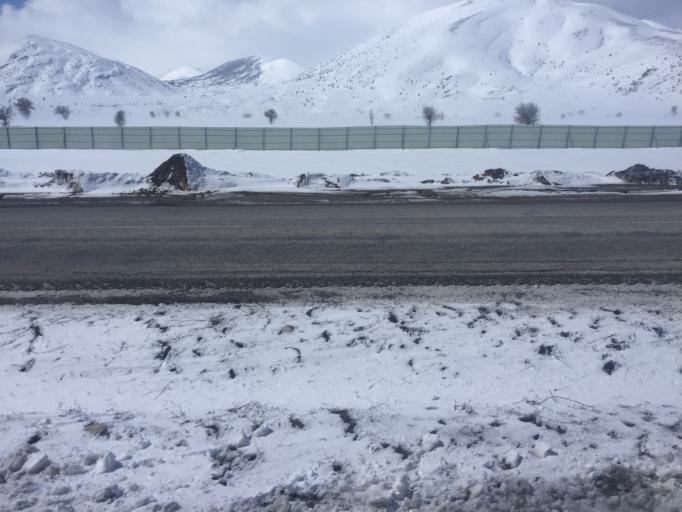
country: TR
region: Kahramanmaras
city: Goksun
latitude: 38.1759
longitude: 36.4603
